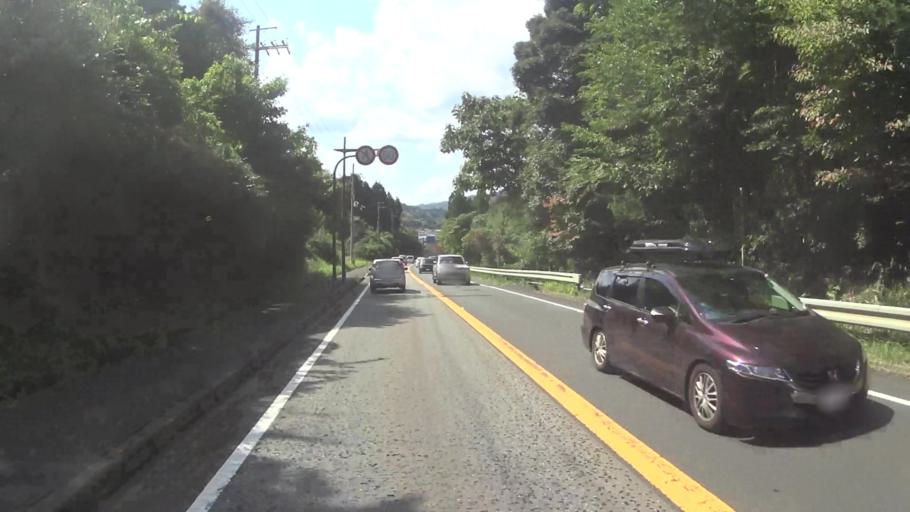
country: JP
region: Kyoto
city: Miyazu
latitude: 35.5520
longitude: 135.1635
